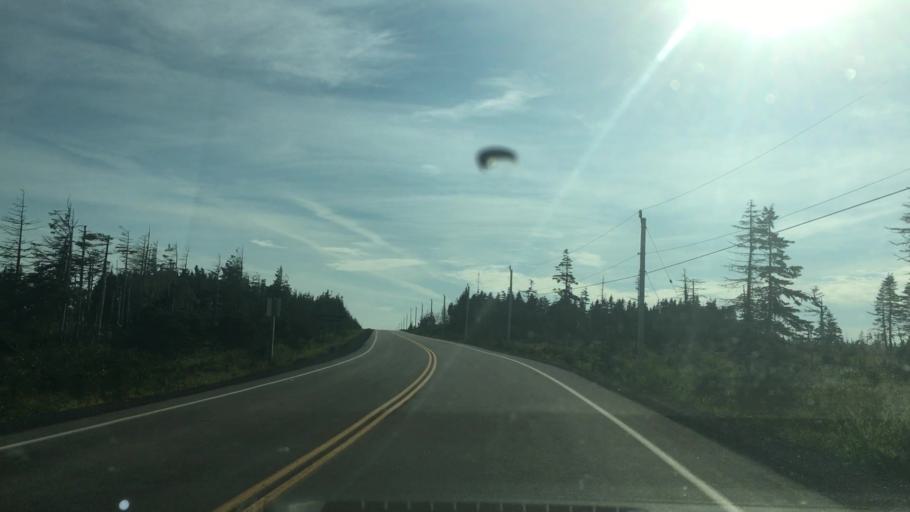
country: CA
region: Nova Scotia
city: Sydney Mines
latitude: 46.8227
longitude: -60.6621
